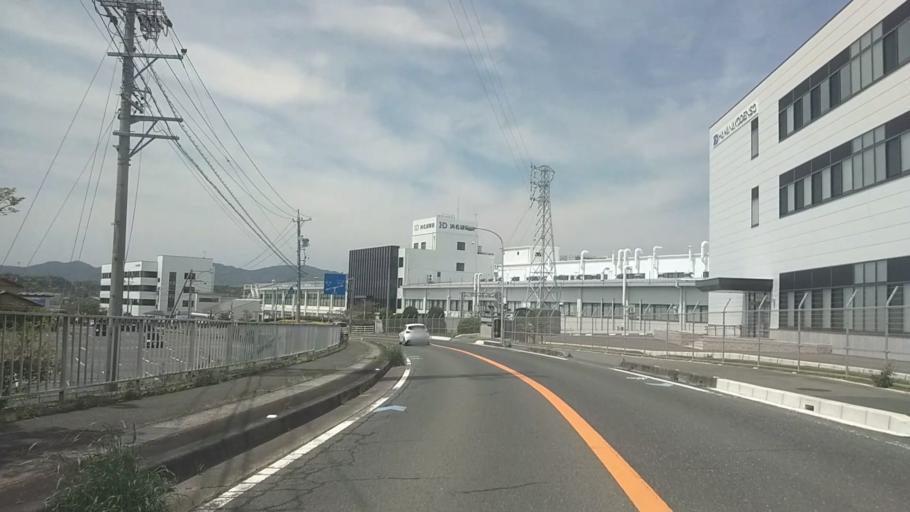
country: JP
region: Shizuoka
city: Kosai-shi
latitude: 34.7220
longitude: 137.5355
